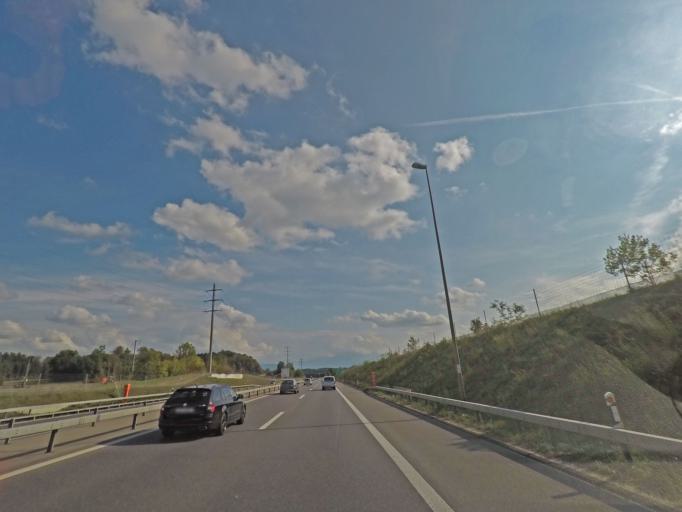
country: CH
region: Zurich
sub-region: Bezirk Affoltern
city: Obfelden / Toussen
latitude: 47.2653
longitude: 8.4402
